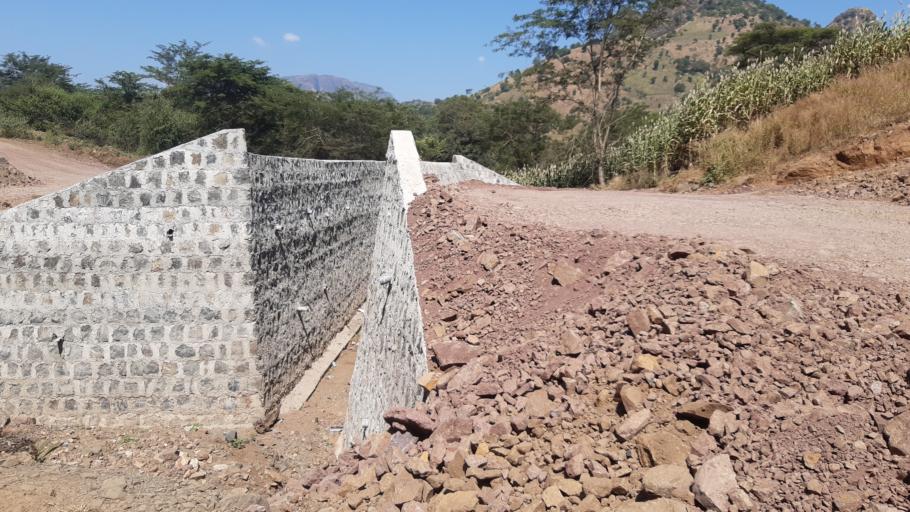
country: ET
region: Amhara
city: Dabat
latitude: 13.1932
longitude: 37.5667
